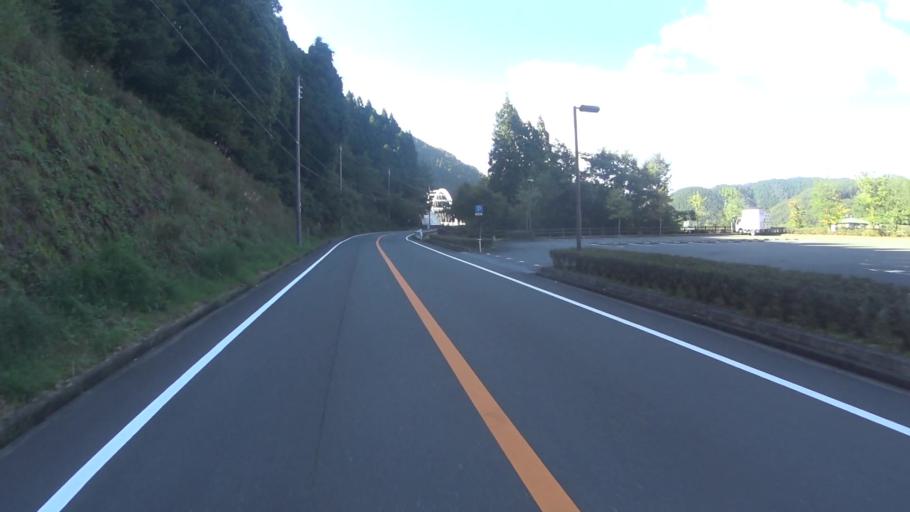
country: JP
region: Kyoto
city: Kameoka
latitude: 35.1430
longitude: 135.5203
